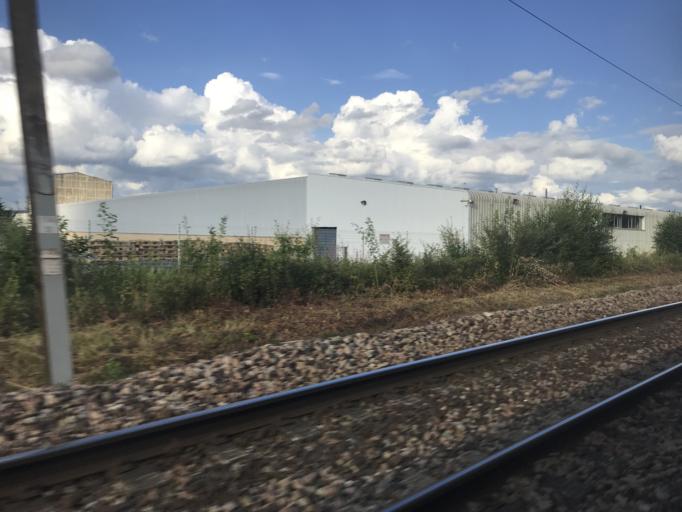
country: FR
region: Champagne-Ardenne
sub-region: Departement des Ardennes
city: Floing
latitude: 49.7037
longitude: 4.9100
